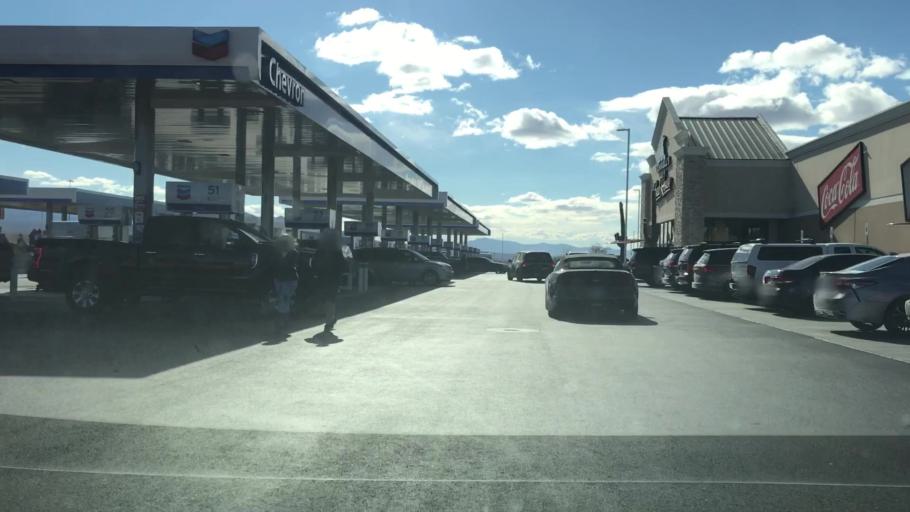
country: US
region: Nevada
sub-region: Clark County
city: Enterprise
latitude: 35.7820
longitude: -115.3322
